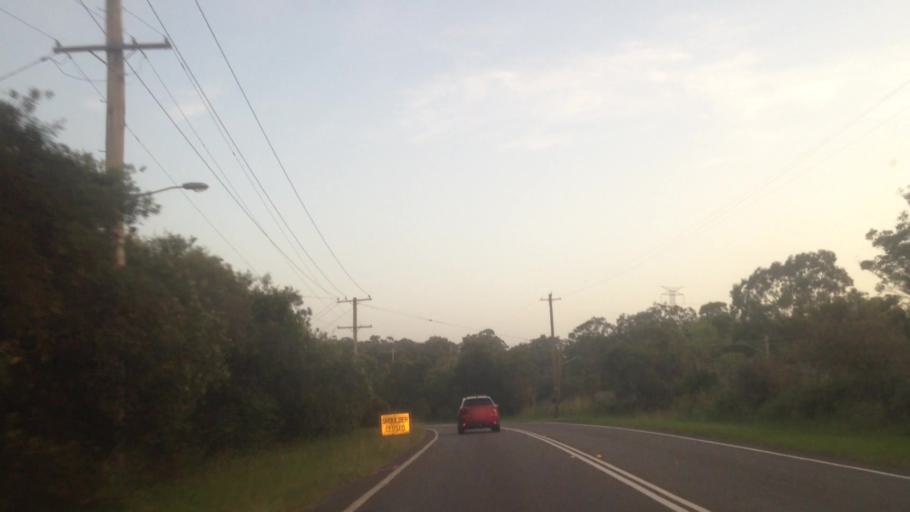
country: AU
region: New South Wales
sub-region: Lake Macquarie Shire
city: Dora Creek
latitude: -33.0963
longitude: 151.4974
